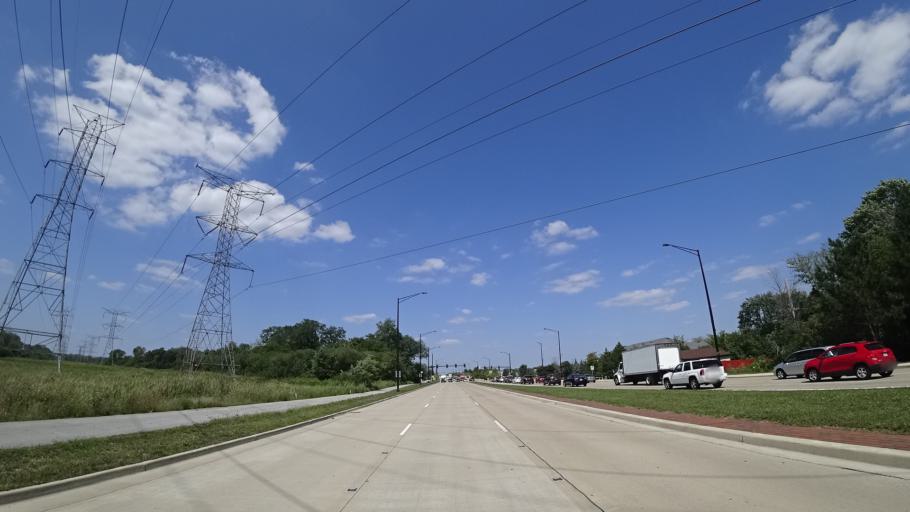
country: US
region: Illinois
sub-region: Cook County
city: Orland Park
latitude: 41.6437
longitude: -87.8540
